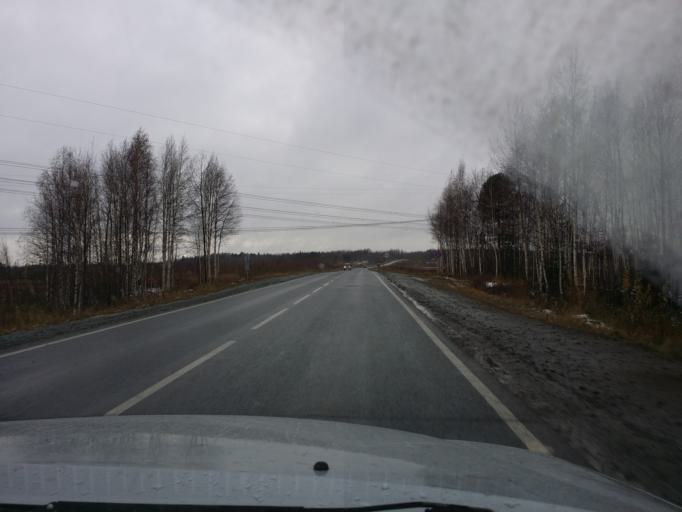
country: RU
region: Khanty-Mansiyskiy Avtonomnyy Okrug
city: Megion
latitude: 61.1078
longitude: 76.0108
